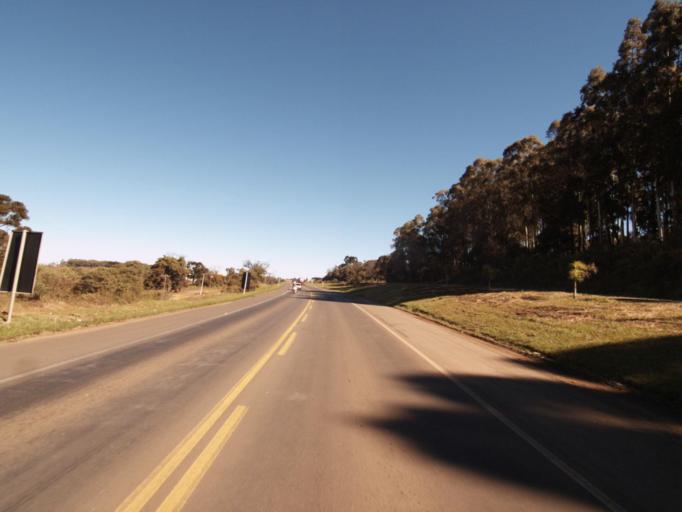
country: BR
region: Santa Catarina
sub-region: Xanxere
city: Xanxere
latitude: -26.8595
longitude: -52.2669
